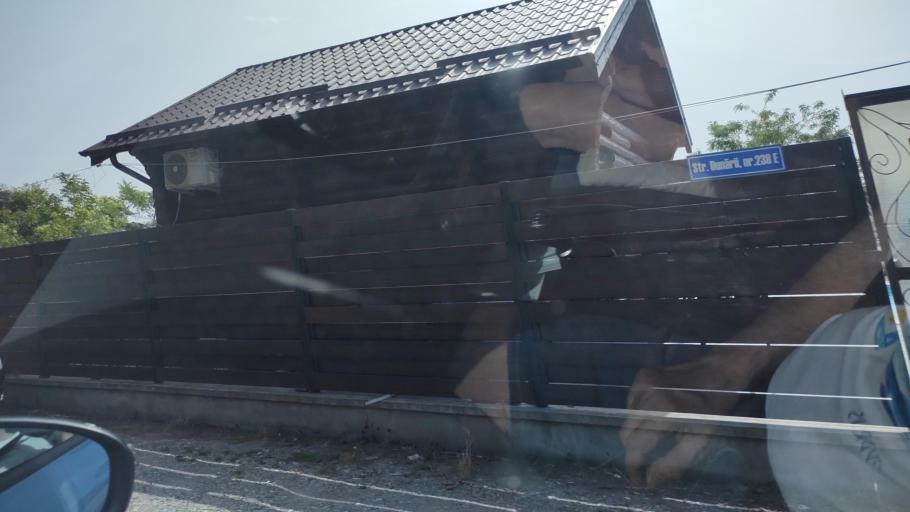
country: RO
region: Mehedinti
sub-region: Comuna Eselnita
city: Eselnita
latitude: 44.6870
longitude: 22.3624
